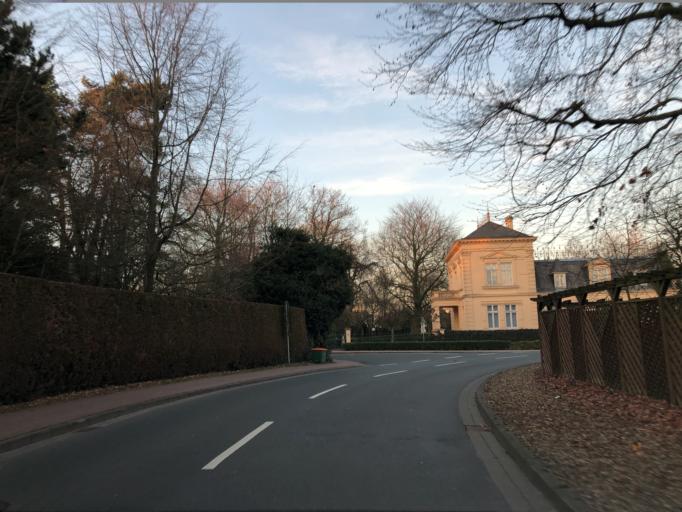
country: DE
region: Lower Saxony
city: Papenburg
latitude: 53.0873
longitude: 7.3906
